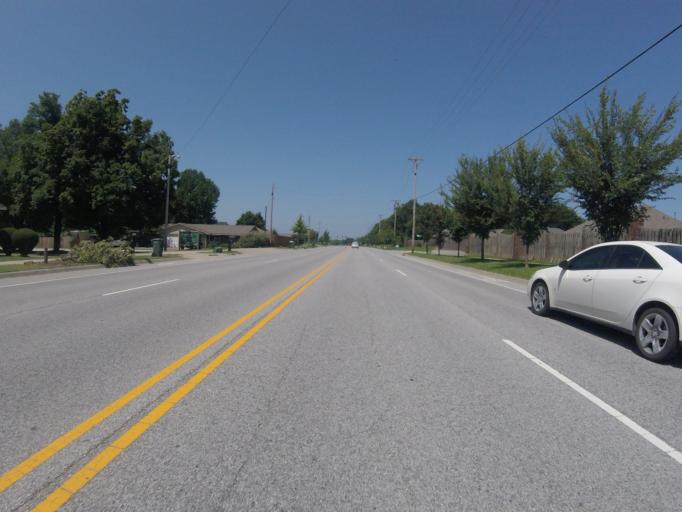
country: US
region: Arkansas
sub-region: Washington County
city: Johnson
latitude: 36.0928
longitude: -94.2051
